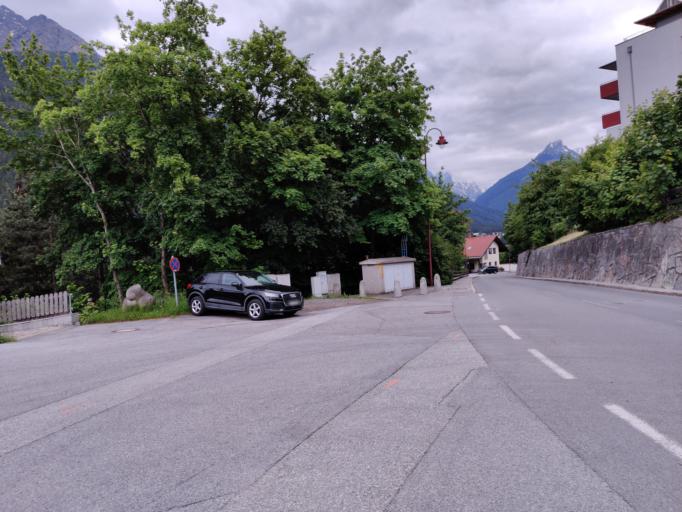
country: AT
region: Tyrol
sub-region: Politischer Bezirk Innsbruck Land
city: Fulpmes
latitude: 47.1551
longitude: 11.3519
